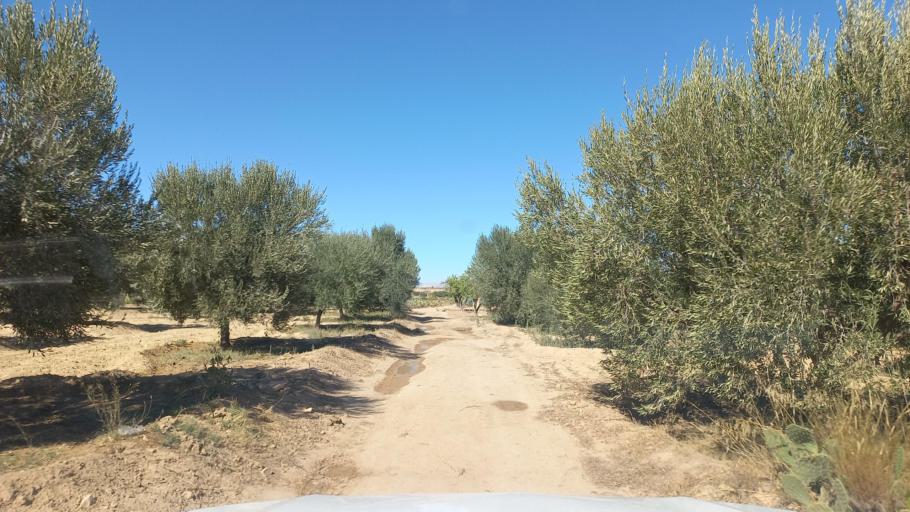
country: TN
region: Al Qasrayn
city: Sbiba
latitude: 35.4009
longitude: 9.0864
